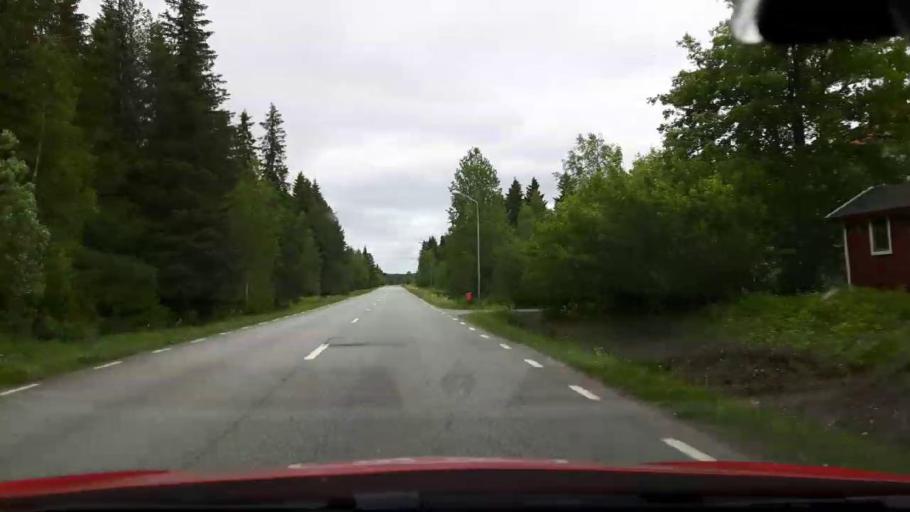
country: SE
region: Jaemtland
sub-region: Stroemsunds Kommun
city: Stroemsund
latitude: 63.5464
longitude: 15.4126
